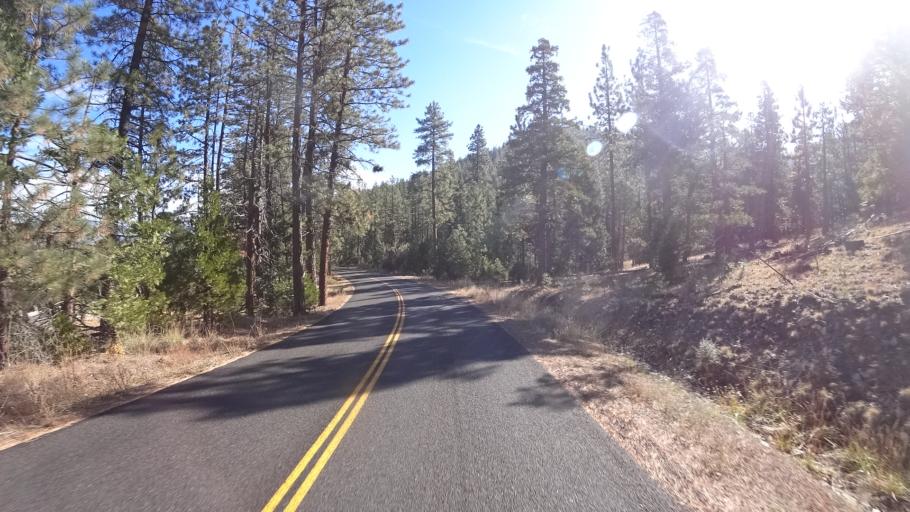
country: US
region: California
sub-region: Siskiyou County
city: Weed
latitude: 41.4326
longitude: -122.4907
